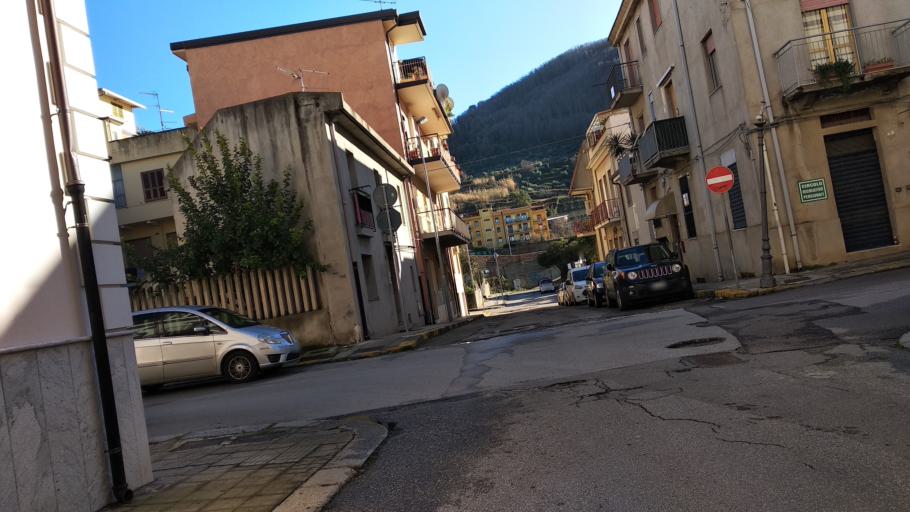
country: IT
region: Calabria
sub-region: Provincia di Reggio Calabria
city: Seminara
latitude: 38.3556
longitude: 15.8460
